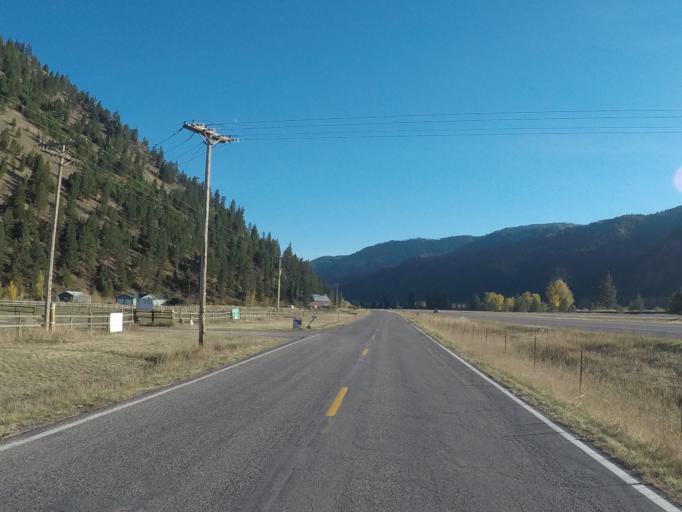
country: US
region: Montana
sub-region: Missoula County
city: Clinton
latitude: 46.7550
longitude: -113.7072
